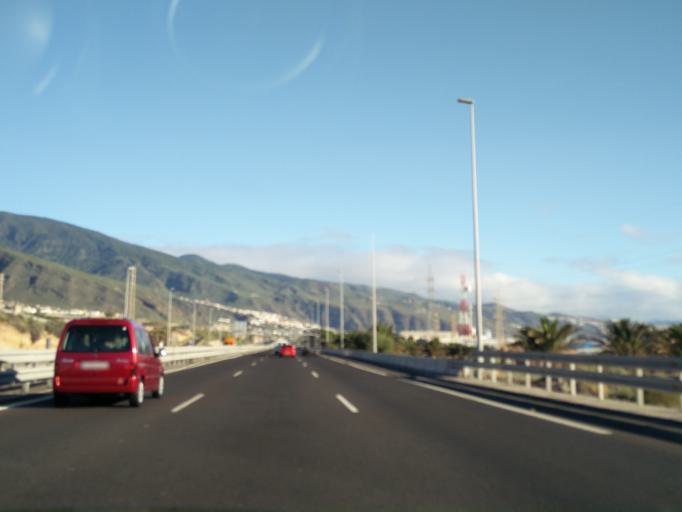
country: ES
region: Canary Islands
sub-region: Provincia de Santa Cruz de Tenerife
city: Candelaria
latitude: 28.3353
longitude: -16.3742
